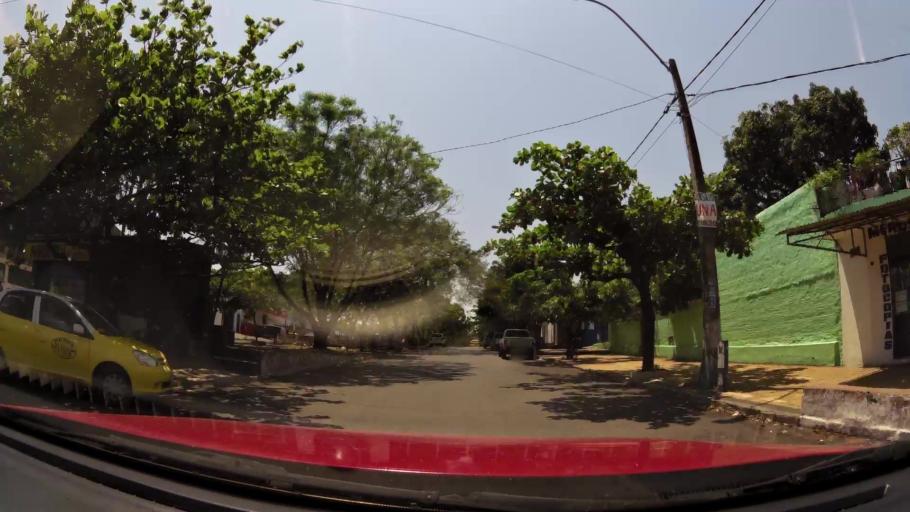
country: PY
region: Asuncion
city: Asuncion
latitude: -25.3080
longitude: -57.6406
